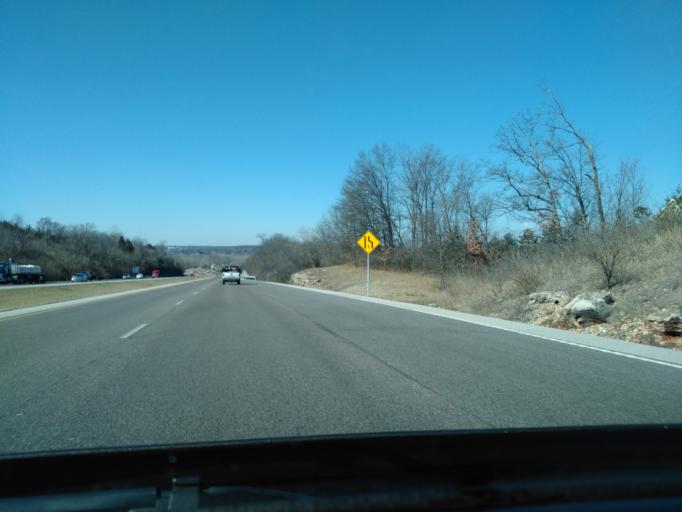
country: US
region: Missouri
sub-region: Saint Louis County
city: Sunset Hills
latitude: 38.5238
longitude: -90.4061
